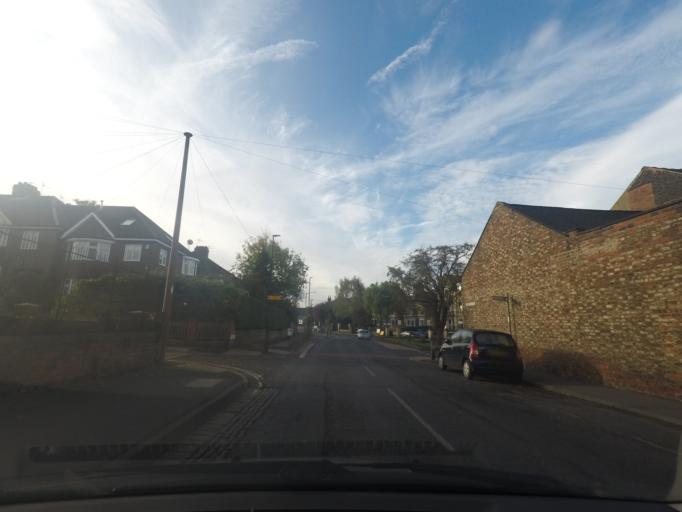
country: GB
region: England
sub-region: City of York
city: York
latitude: 53.9491
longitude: -1.0736
